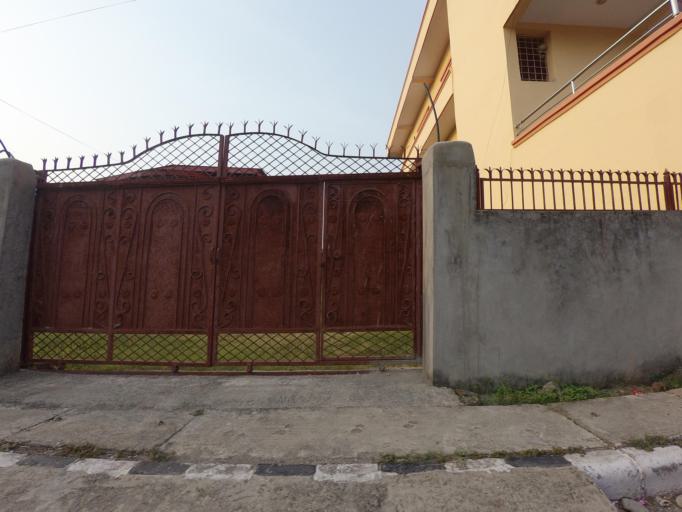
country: NP
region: Western Region
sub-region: Lumbini Zone
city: Bhairahawa
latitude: 27.5112
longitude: 83.4564
